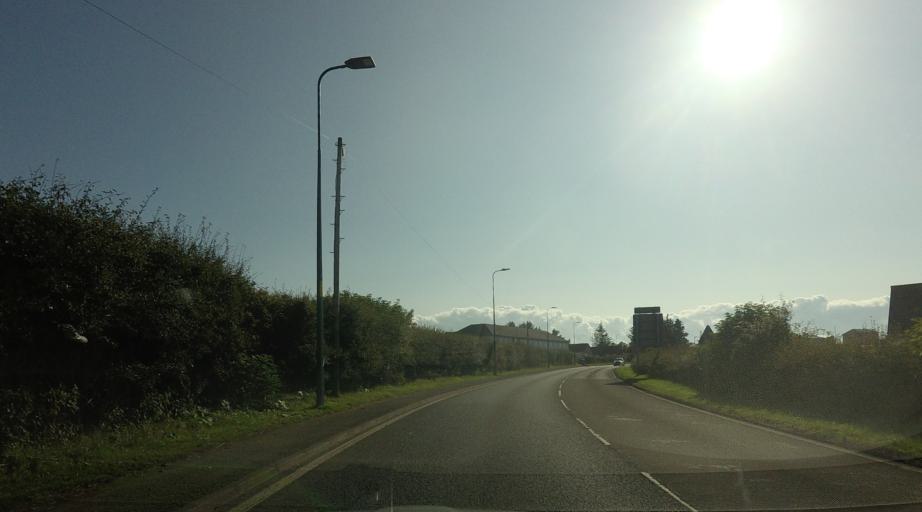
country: GB
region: Scotland
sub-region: Highland
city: Thurso
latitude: 58.5908
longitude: -3.5165
